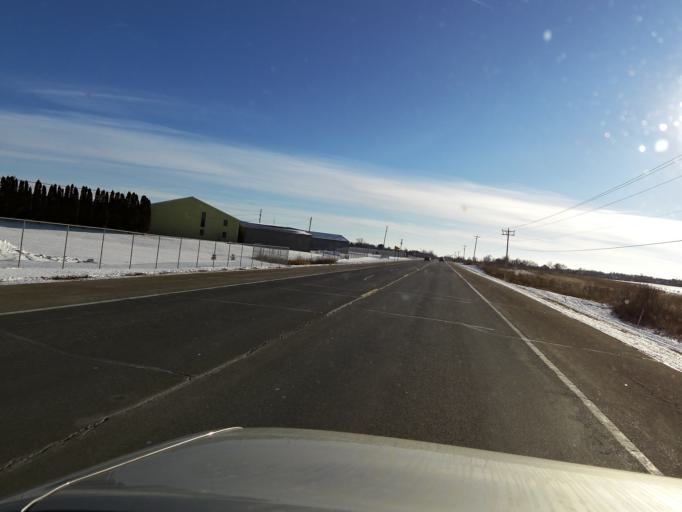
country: US
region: Minnesota
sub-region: Washington County
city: Lake Elmo
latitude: 44.9991
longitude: -92.8629
